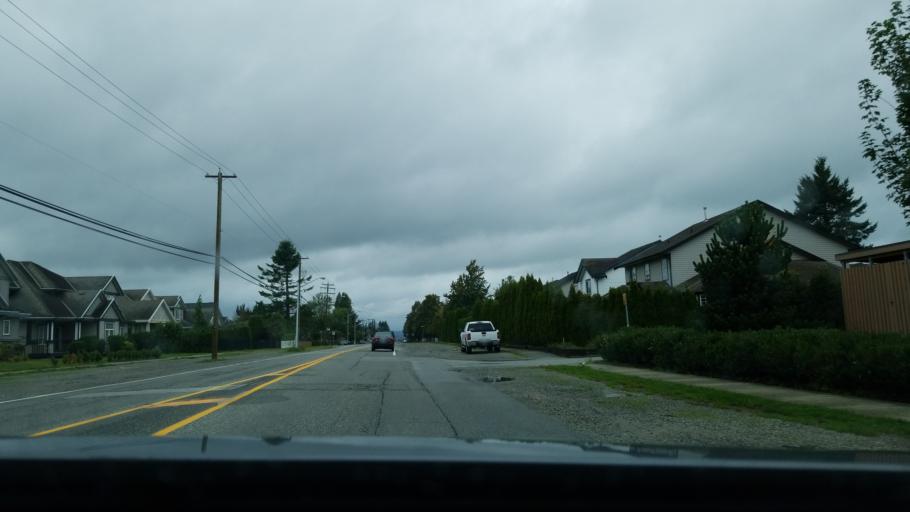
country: CA
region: British Columbia
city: Langley
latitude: 49.1189
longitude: -122.7049
